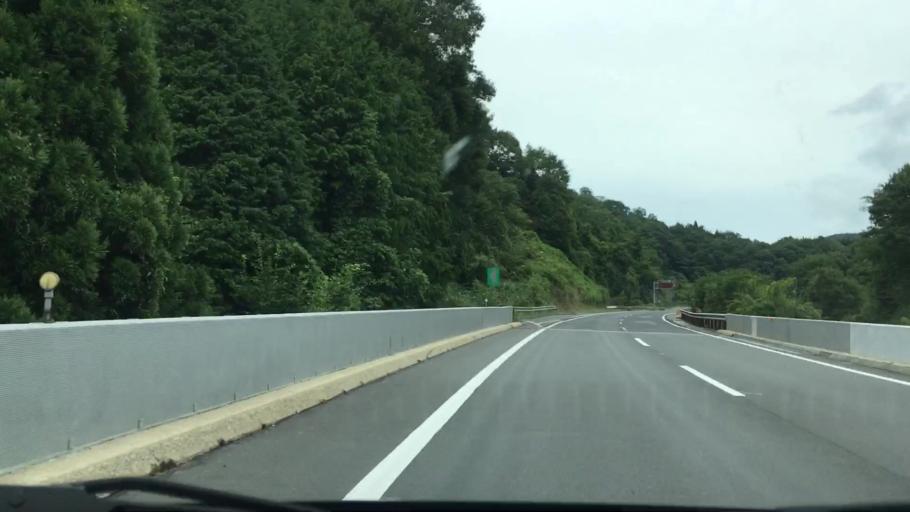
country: JP
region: Okayama
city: Niimi
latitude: 34.9798
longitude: 133.6161
